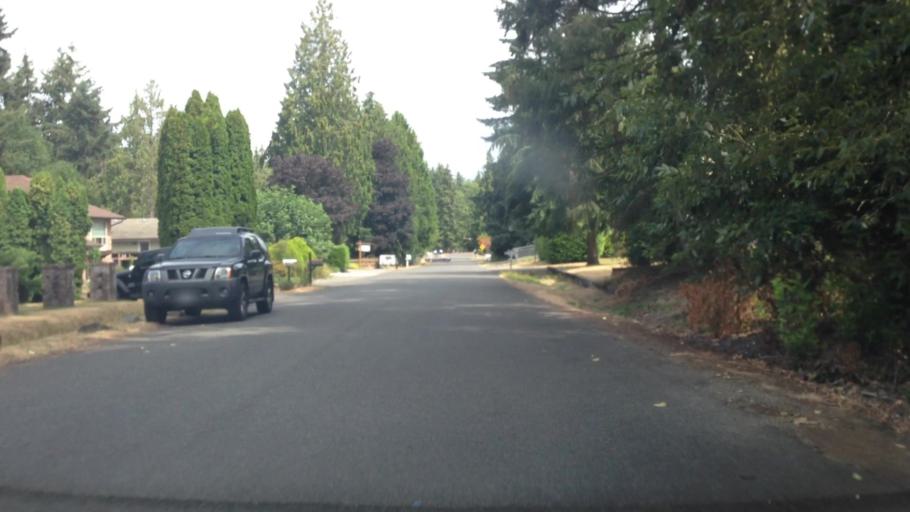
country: US
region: Washington
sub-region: Pierce County
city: South Hill
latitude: 47.1131
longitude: -122.2983
